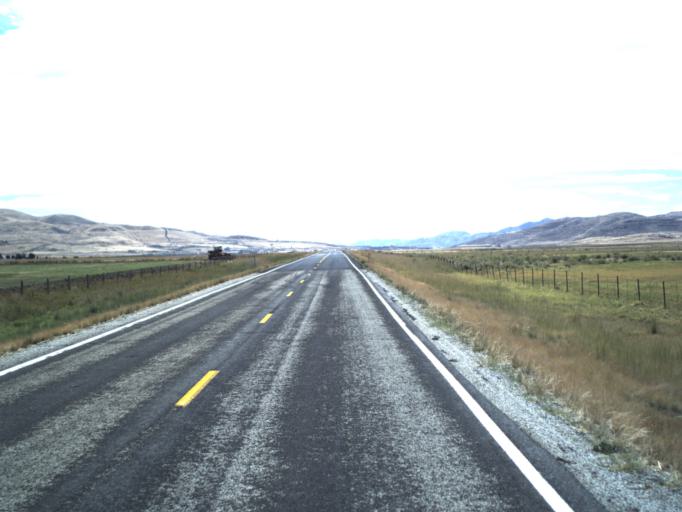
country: US
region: Utah
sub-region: Box Elder County
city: Tremonton
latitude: 41.7547
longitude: -112.4347
